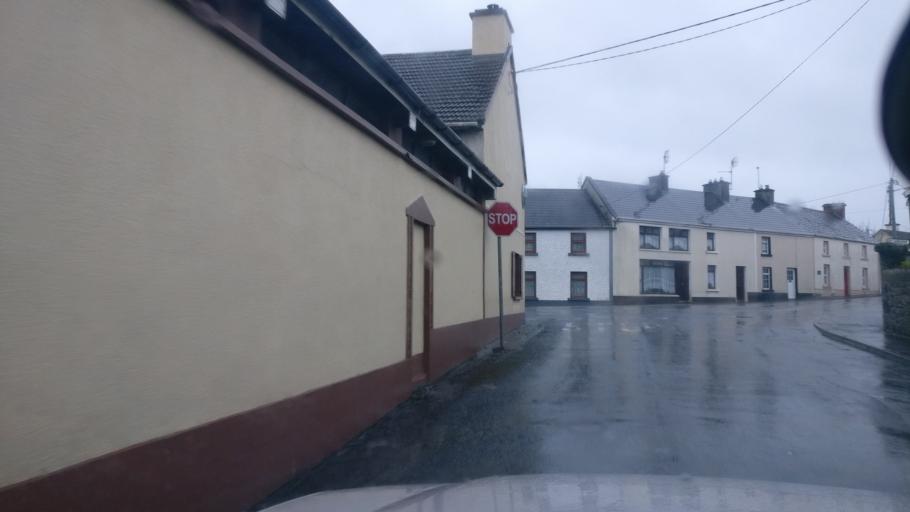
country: IE
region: Connaught
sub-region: County Galway
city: Ballinasloe
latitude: 53.3040
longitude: -8.3175
